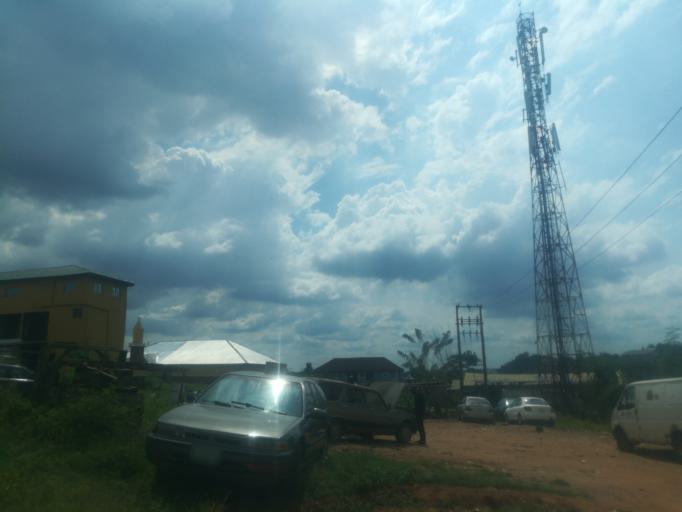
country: NG
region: Oyo
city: Ibadan
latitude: 7.4184
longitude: 3.8566
